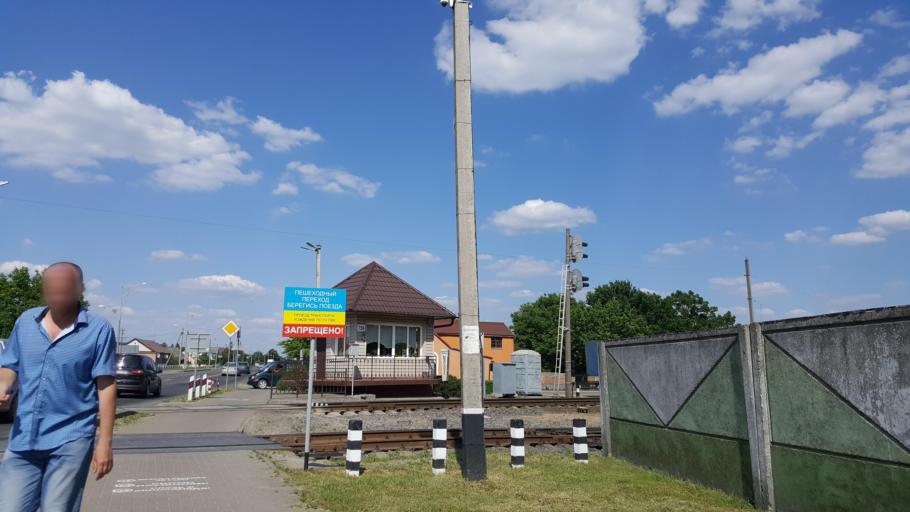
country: BY
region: Brest
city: Horad Kobryn
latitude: 52.2212
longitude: 24.3643
